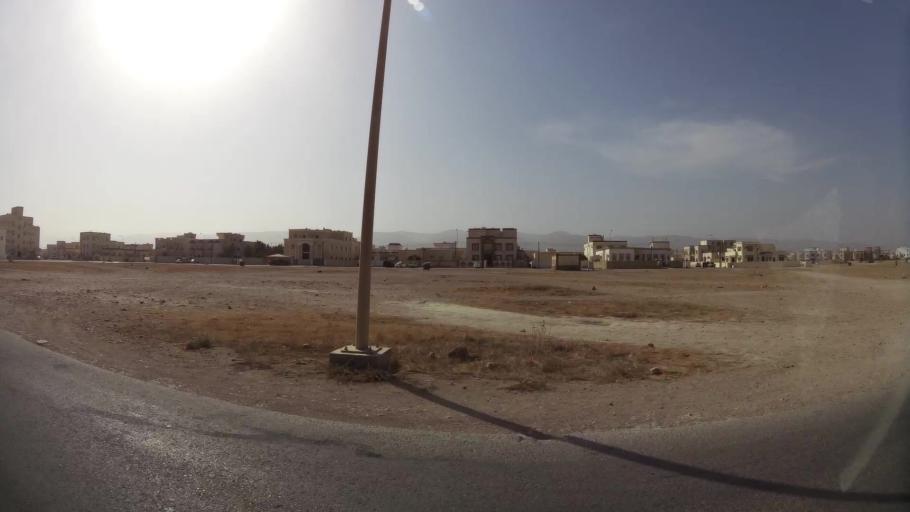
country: OM
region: Zufar
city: Salalah
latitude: 17.0107
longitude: 54.0133
